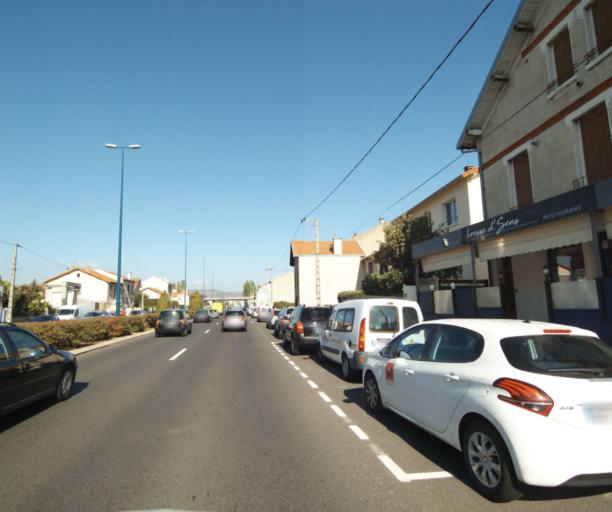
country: FR
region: Auvergne
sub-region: Departement du Puy-de-Dome
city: Aubiere
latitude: 45.7696
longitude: 3.1236
